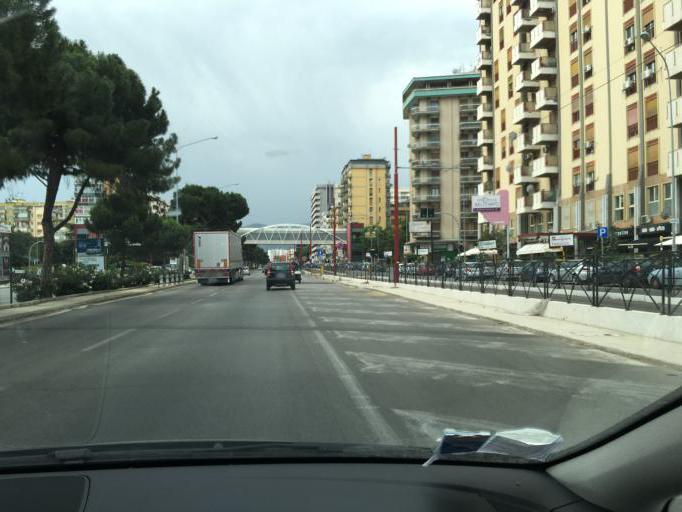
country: IT
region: Sicily
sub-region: Palermo
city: Palermo
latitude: 38.1265
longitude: 13.3294
